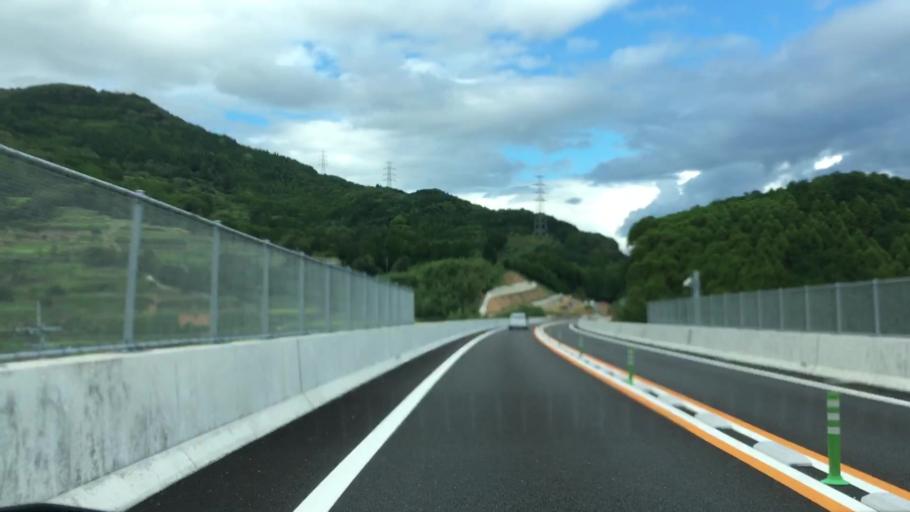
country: JP
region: Saga Prefecture
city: Imaricho-ko
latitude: 33.3110
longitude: 129.9173
